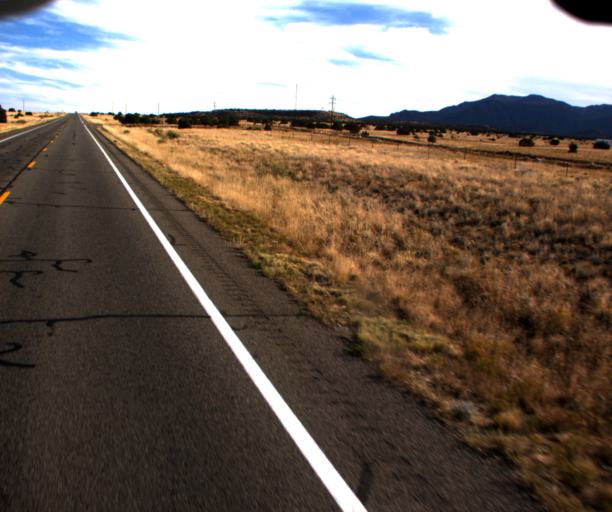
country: US
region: New Mexico
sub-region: San Juan County
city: Shiprock
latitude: 36.9010
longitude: -109.0673
